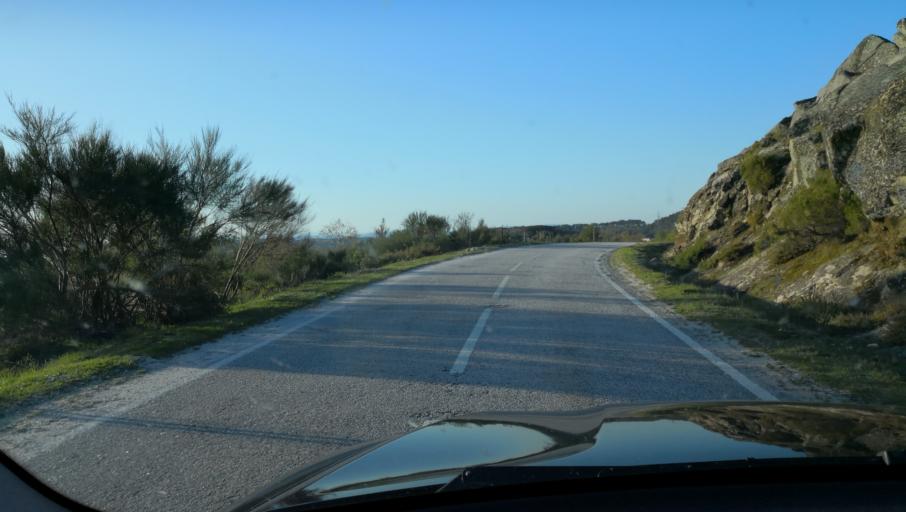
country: PT
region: Vila Real
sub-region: Vila Real
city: Vila Real
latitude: 41.3905
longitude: -7.8273
